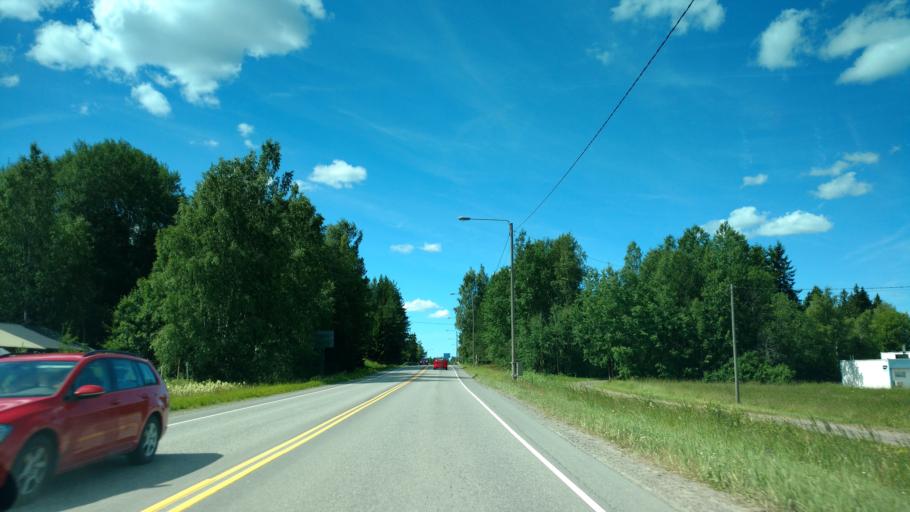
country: FI
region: Varsinais-Suomi
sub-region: Turku
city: Lieto
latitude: 60.4523
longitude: 22.4549
